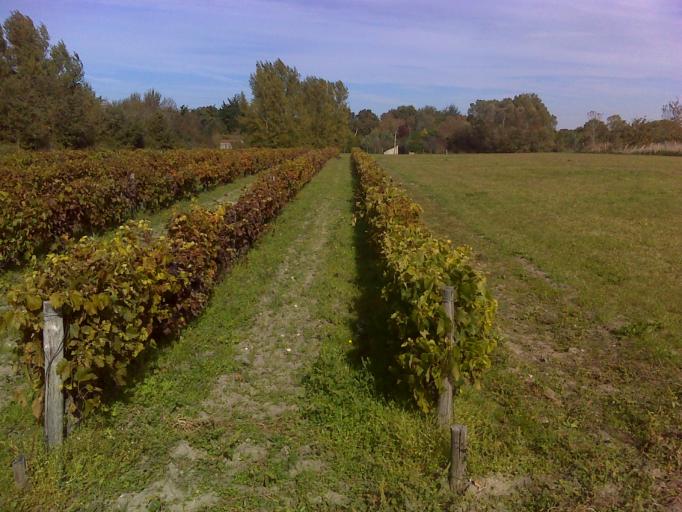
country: FR
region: Poitou-Charentes
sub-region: Departement de la Charente-Maritime
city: Marennes
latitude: 45.8354
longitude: -1.1042
